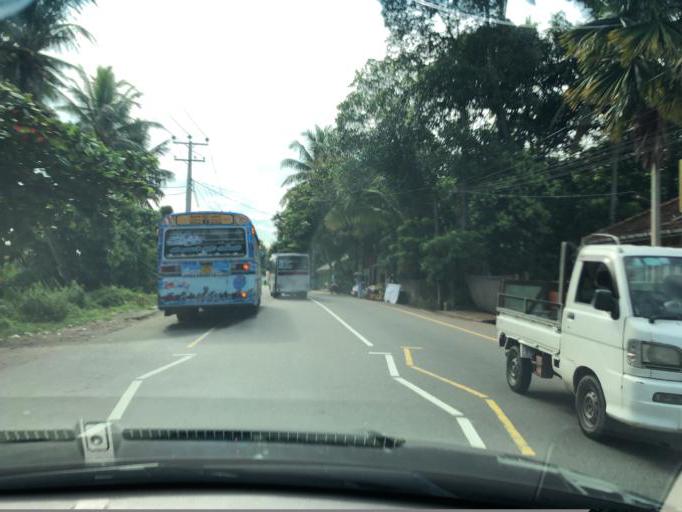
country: LK
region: Western
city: Kalutara
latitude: 6.5684
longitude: 79.9895
